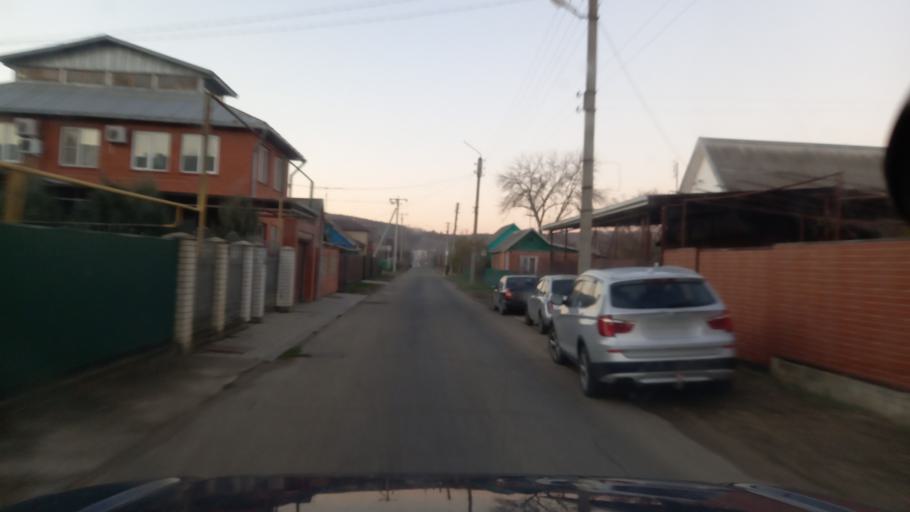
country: RU
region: Krasnodarskiy
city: Goryachiy Klyuch
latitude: 44.6293
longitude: 39.1042
